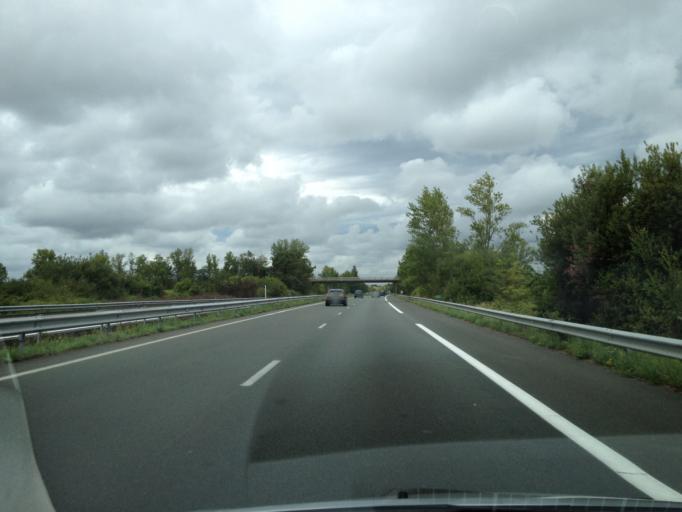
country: FR
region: Aquitaine
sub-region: Departement du Lot-et-Garonne
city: Meilhan-sur-Garonne
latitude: 44.4667
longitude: 0.0629
